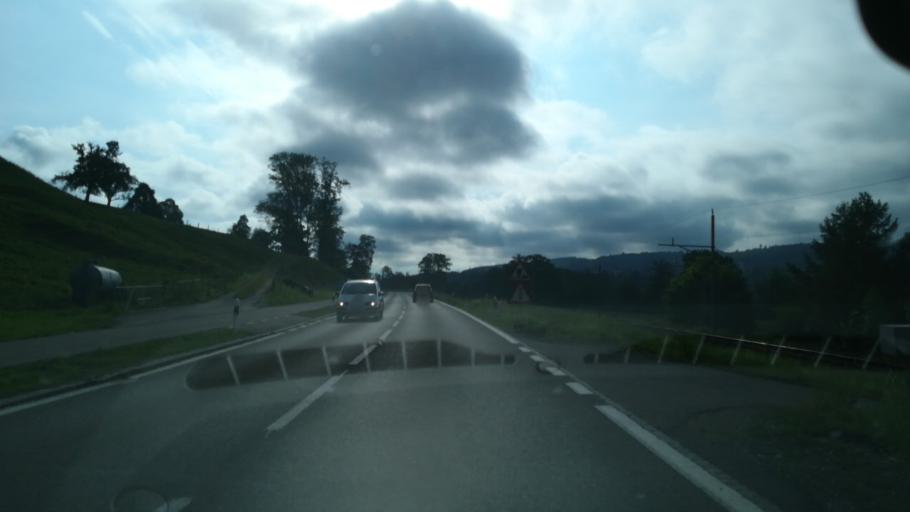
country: CH
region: Saint Gallen
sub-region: Wahlkreis Wil
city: Niederburen
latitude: 47.4975
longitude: 9.2221
